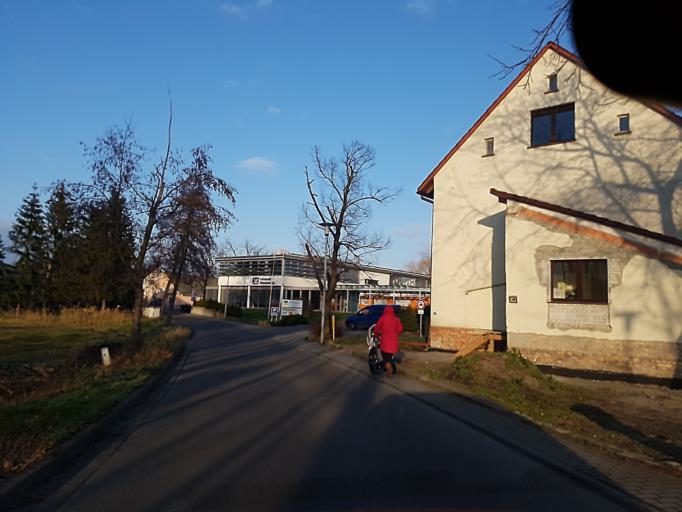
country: DE
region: Brandenburg
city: Bad Liebenwerda
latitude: 51.5162
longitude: 13.4119
